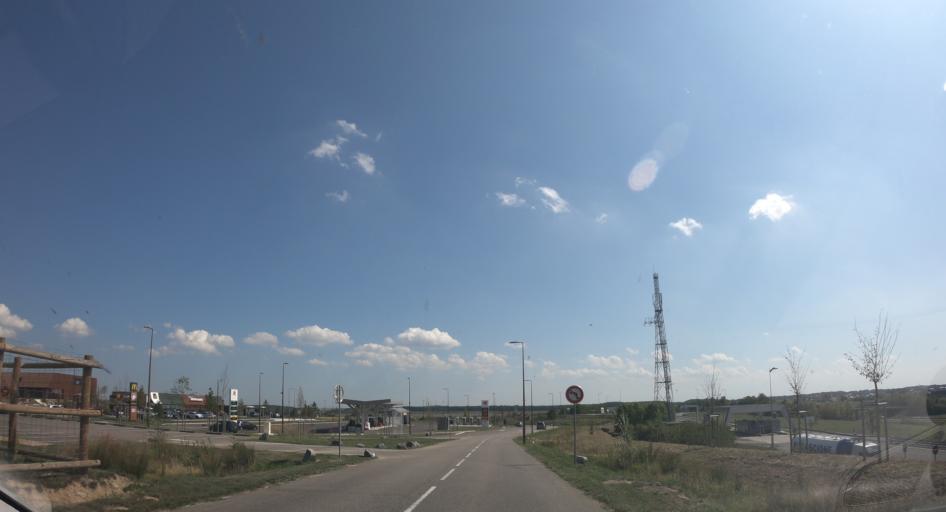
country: FR
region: Lorraine
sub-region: Departement de la Moselle
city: Farebersviller
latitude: 49.1103
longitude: 6.8556
